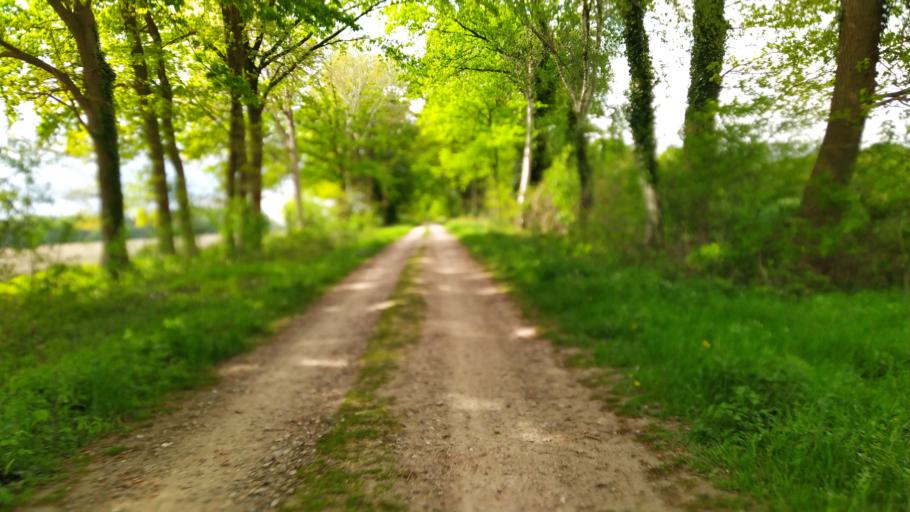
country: DE
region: Lower Saxony
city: Farven
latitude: 53.4273
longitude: 9.3427
